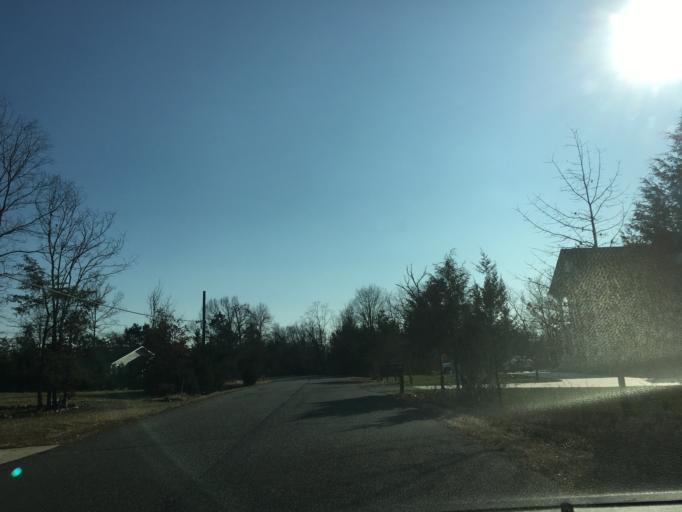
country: US
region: Virginia
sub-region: Fairfax County
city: Fairfax Station
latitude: 38.8258
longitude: -77.3716
